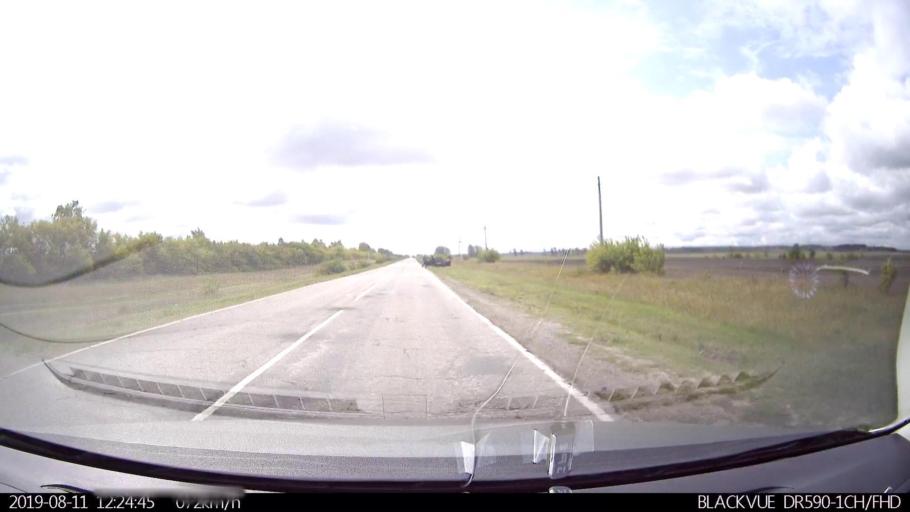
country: RU
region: Ulyanovsk
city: Ignatovka
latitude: 53.8802
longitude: 47.9461
